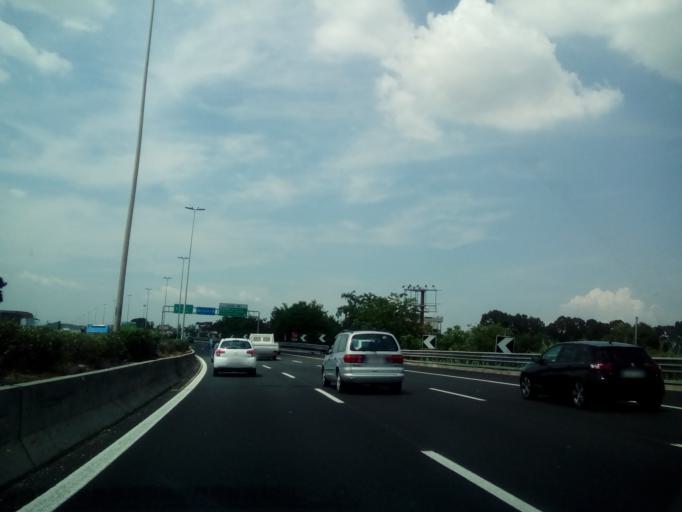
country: IT
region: Latium
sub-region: Citta metropolitana di Roma Capitale
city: Setteville
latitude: 41.9147
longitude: 12.6157
